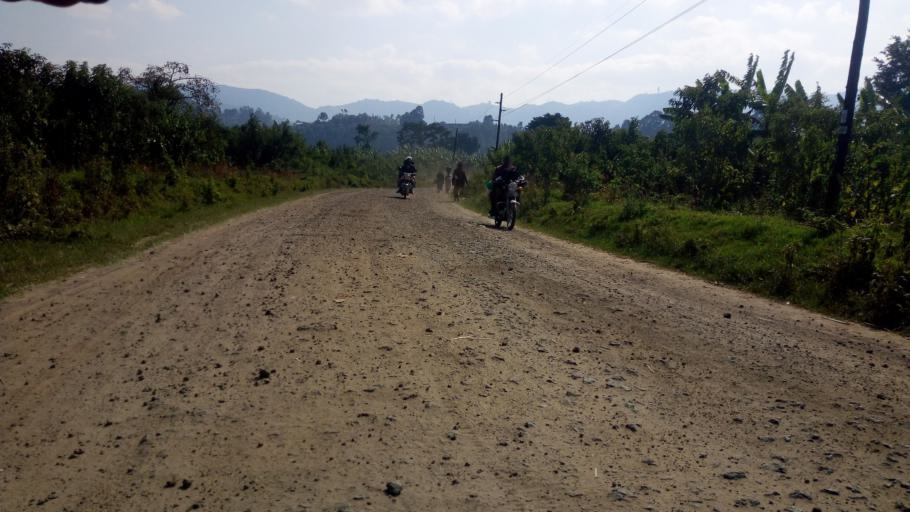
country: UG
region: Western Region
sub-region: Kisoro District
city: Kisoro
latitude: -1.2262
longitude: 29.7129
